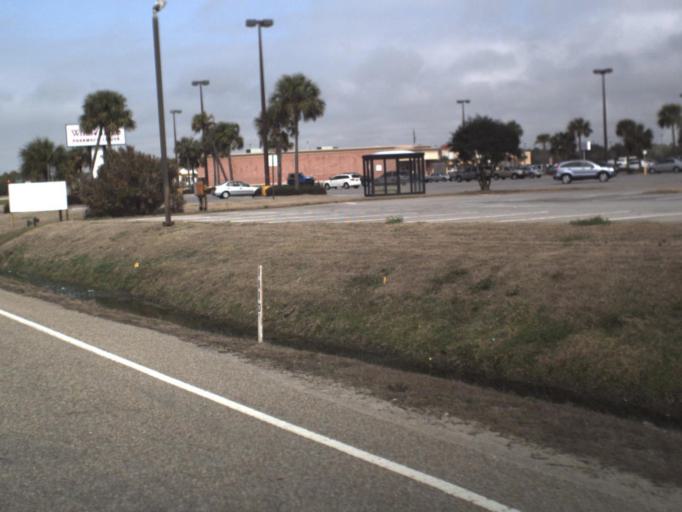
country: US
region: Florida
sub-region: Bay County
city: Laguna Beach
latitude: 30.2623
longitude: -85.9748
